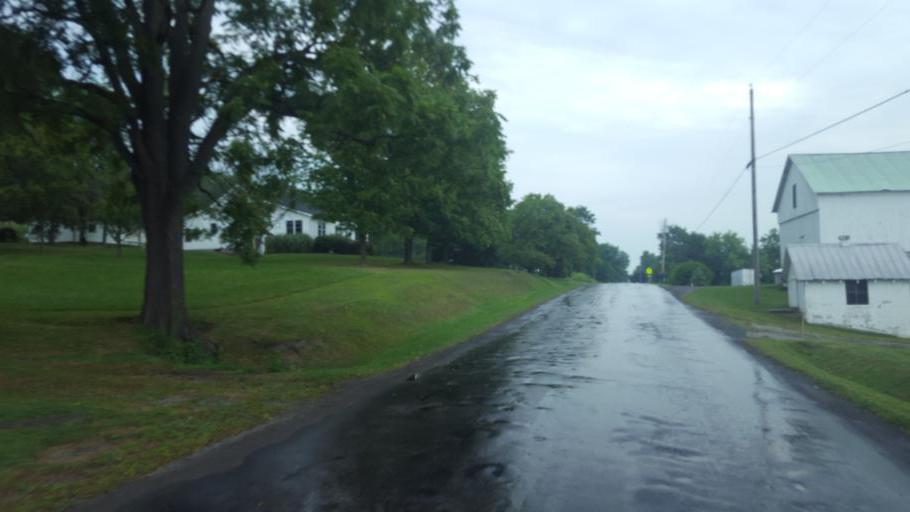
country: US
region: Ohio
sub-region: Geauga County
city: Middlefield
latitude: 41.4353
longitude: -80.9970
